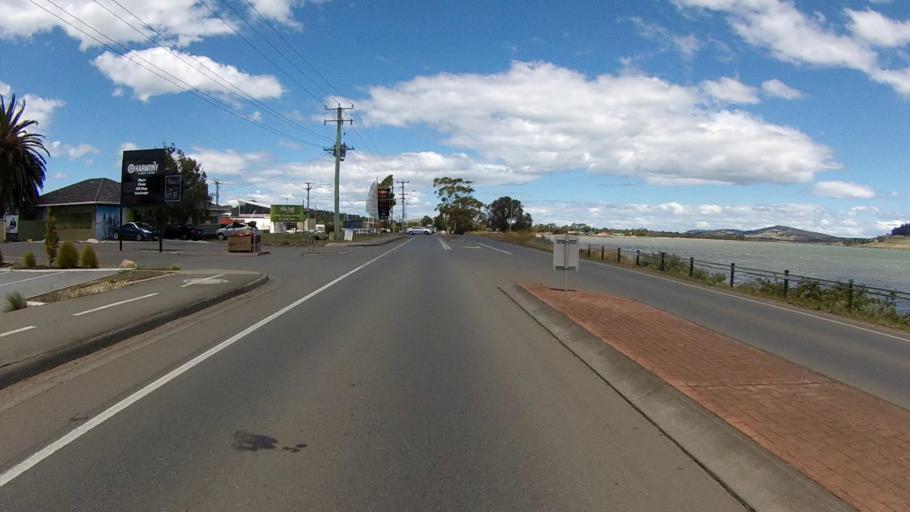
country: AU
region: Tasmania
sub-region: Clarence
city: Lauderdale
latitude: -42.9075
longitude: 147.4813
